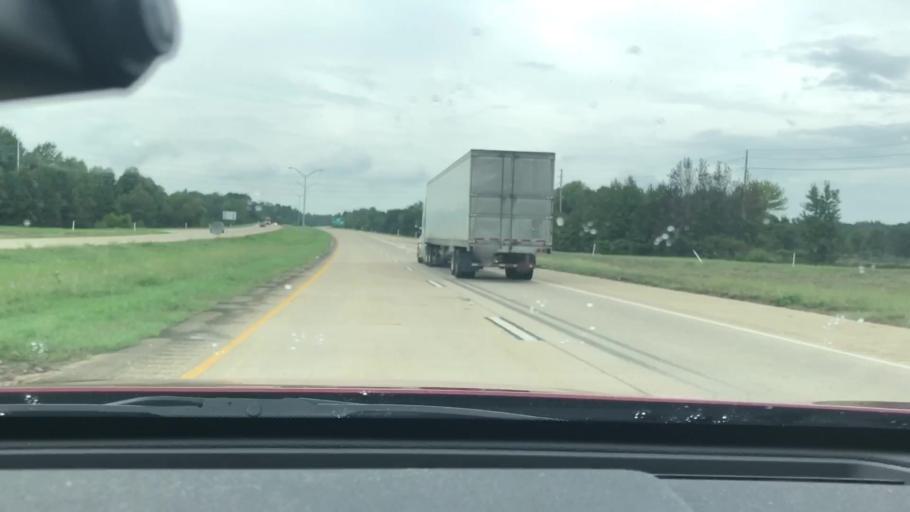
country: US
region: Texas
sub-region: Bowie County
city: Texarkana
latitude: 33.3859
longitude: -94.0462
